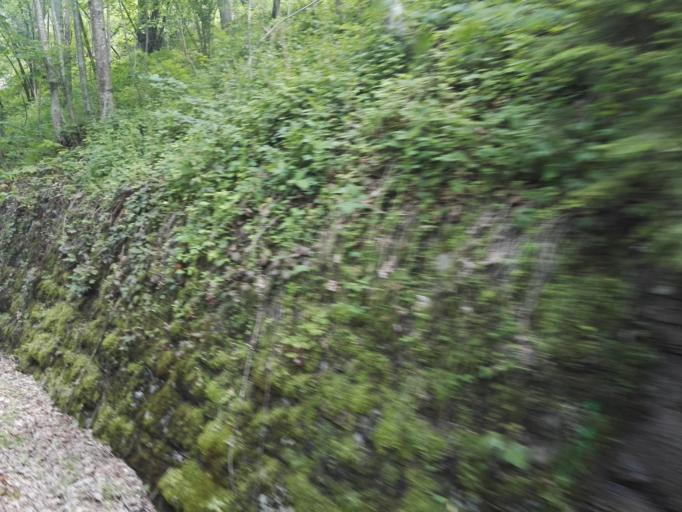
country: AT
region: Styria
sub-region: Politischer Bezirk Weiz
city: Koglhof
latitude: 47.3124
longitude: 15.6943
